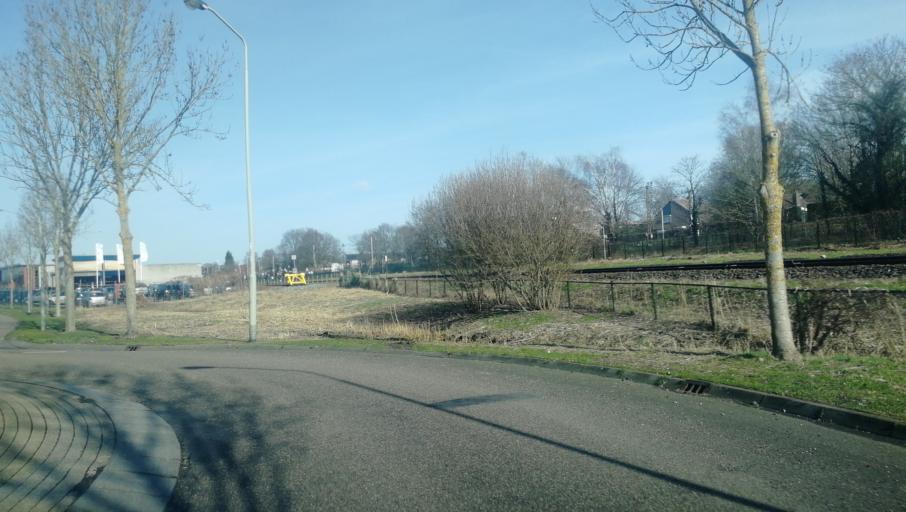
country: NL
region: Limburg
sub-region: Gemeente Venlo
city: Venlo
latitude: 51.3540
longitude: 6.1749
